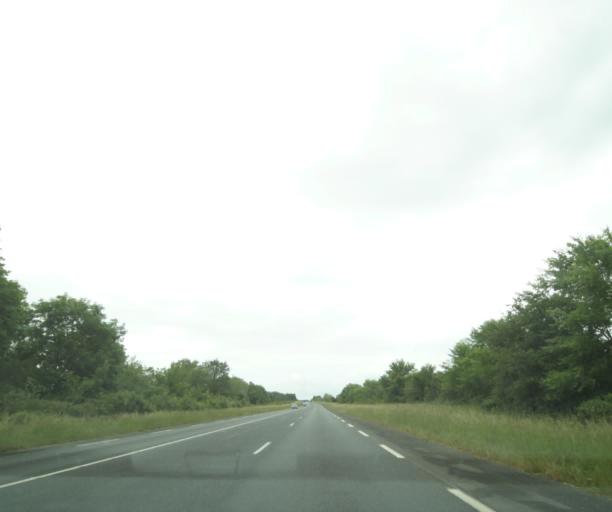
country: FR
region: Poitou-Charentes
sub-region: Departement des Deux-Sevres
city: Saint-Varent
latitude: 46.8513
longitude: -0.2087
